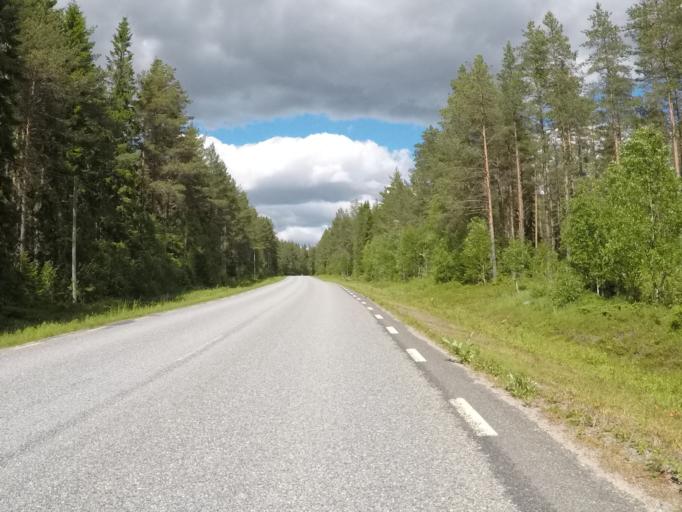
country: SE
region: Vaesterbotten
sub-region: Robertsfors Kommun
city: Robertsfors
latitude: 63.9709
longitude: 20.8117
